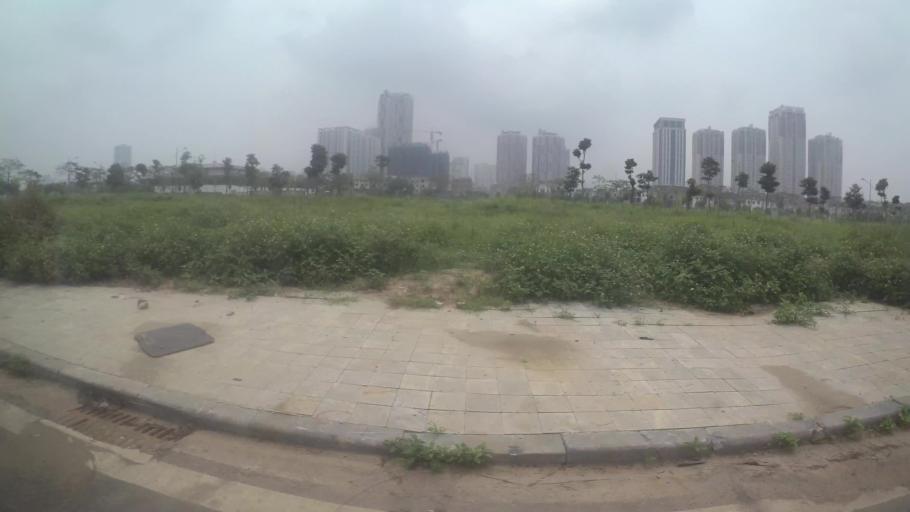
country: VN
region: Ha Noi
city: Ha Dong
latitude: 20.9786
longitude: 105.7560
